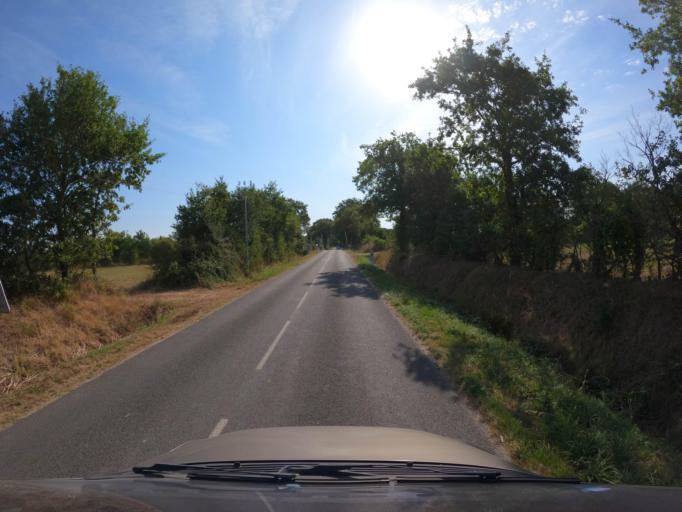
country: FR
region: Pays de la Loire
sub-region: Departement de la Vendee
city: Soullans
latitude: 46.8052
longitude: -1.8874
